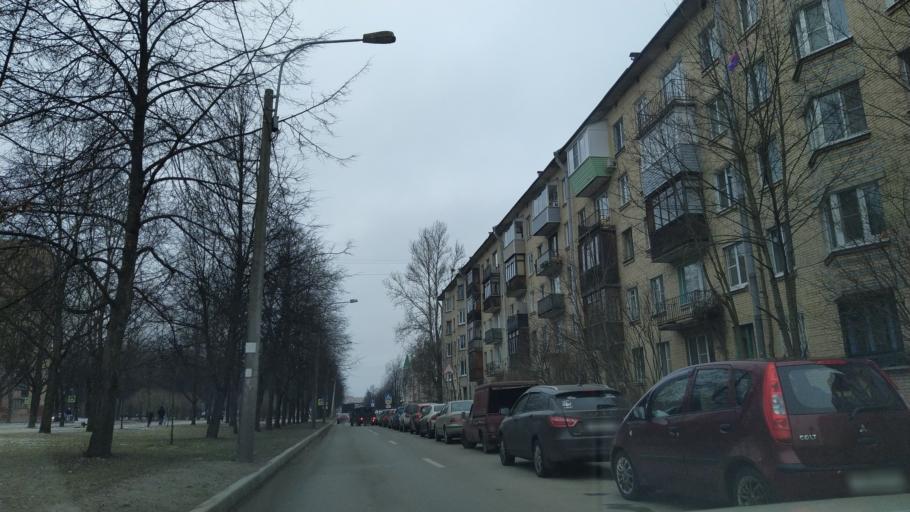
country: RU
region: St.-Petersburg
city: Pushkin
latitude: 59.7320
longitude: 30.4164
